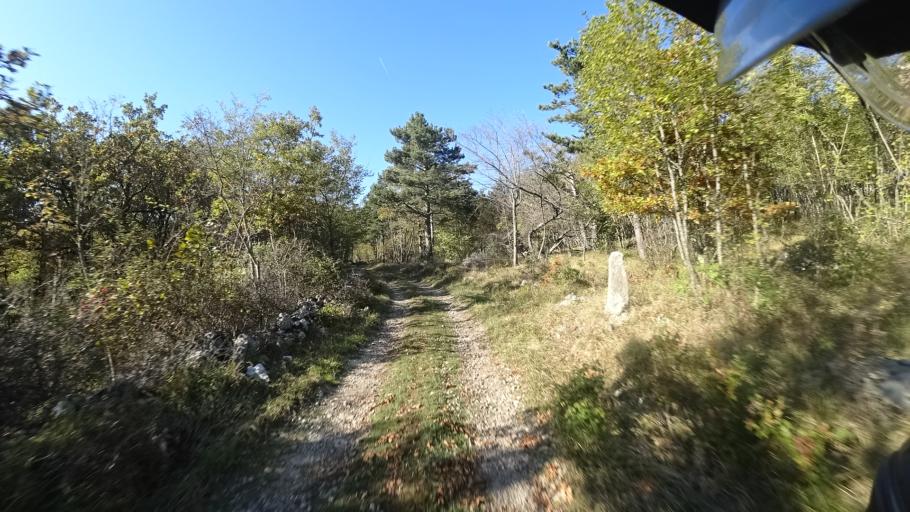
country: HR
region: Primorsko-Goranska
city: Klana
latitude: 45.4515
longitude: 14.3446
